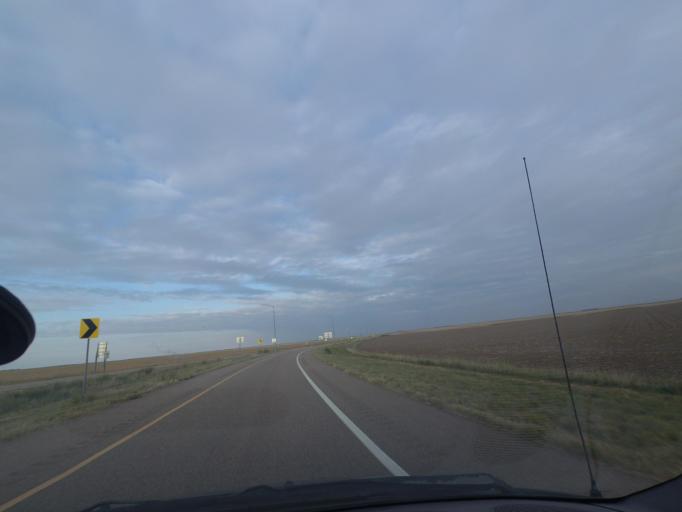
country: US
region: Colorado
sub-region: Yuma County
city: Wray
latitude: 39.7458
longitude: -102.2528
